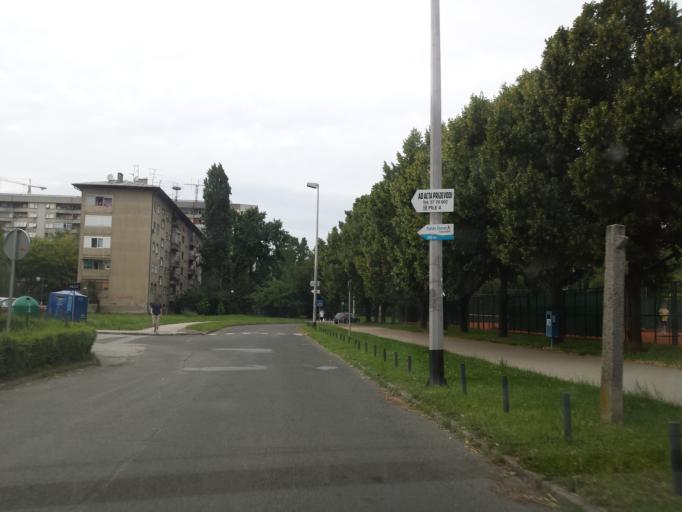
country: HR
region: Grad Zagreb
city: Novi Zagreb
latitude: 45.7988
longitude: 15.9927
